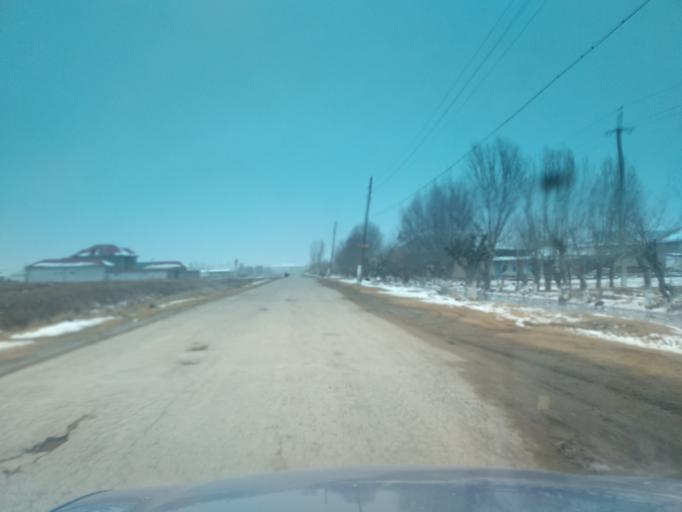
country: UZ
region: Sirdaryo
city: Guliston
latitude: 40.4796
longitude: 68.7510
